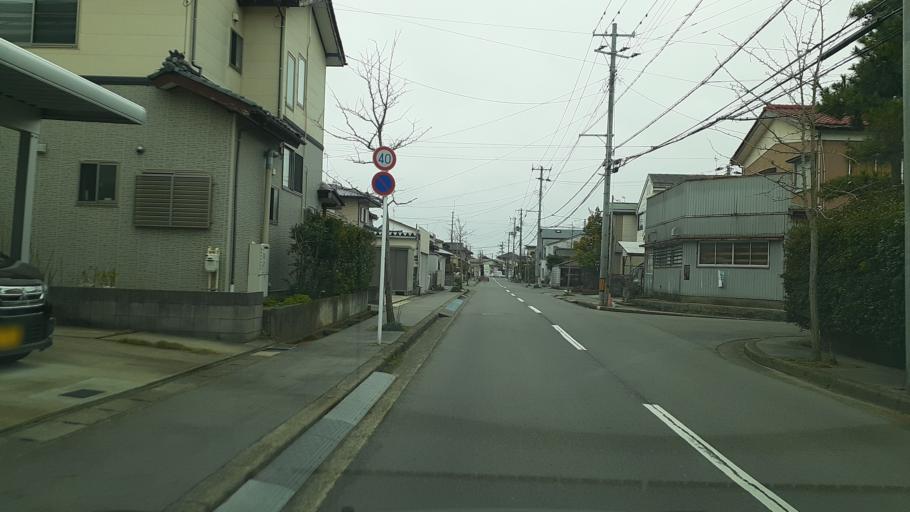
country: JP
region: Niigata
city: Niigata-shi
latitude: 37.8613
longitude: 139.0390
